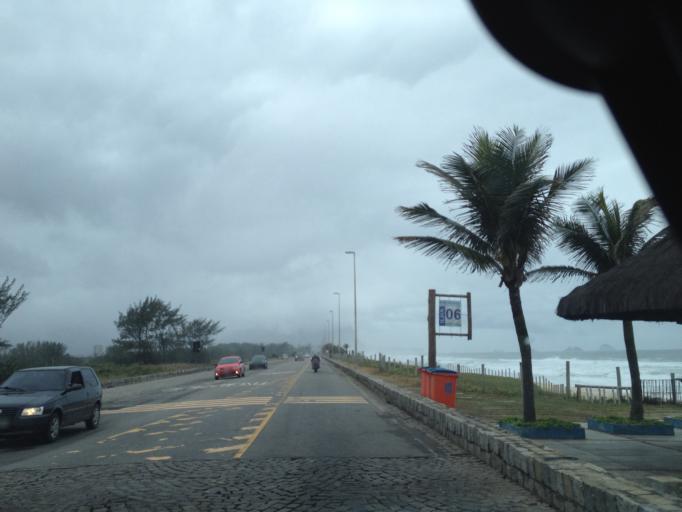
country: BR
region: Rio de Janeiro
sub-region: Nilopolis
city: Nilopolis
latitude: -23.0155
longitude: -43.4114
